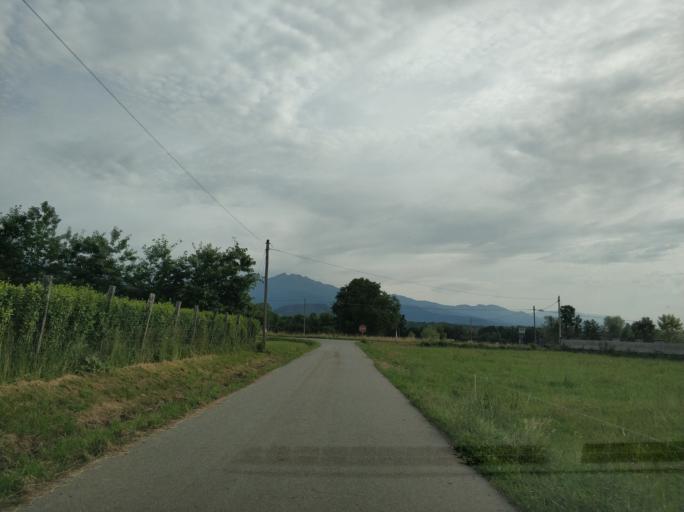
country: IT
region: Piedmont
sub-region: Provincia di Torino
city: Vauda Canavese Superiore
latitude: 45.2978
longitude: 7.6139
